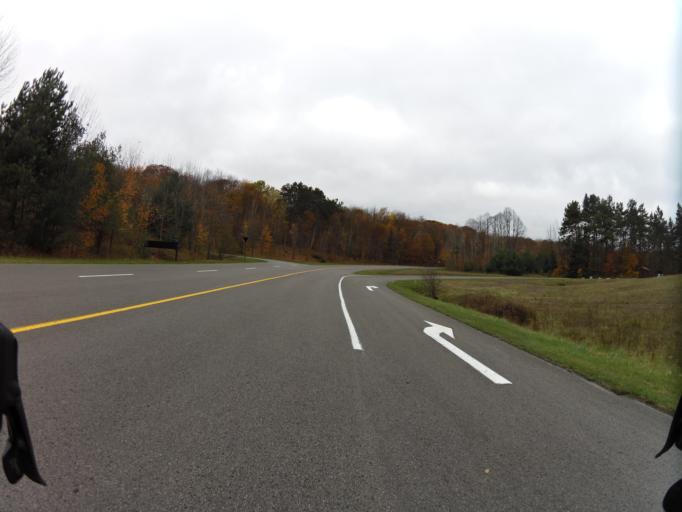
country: CA
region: Quebec
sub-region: Outaouais
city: Gatineau
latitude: 45.4957
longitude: -75.8322
